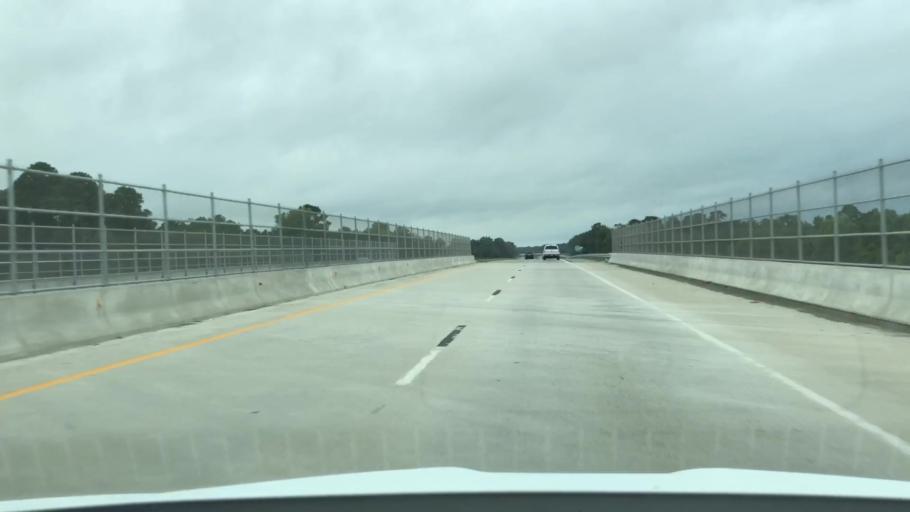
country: US
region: North Carolina
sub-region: Wayne County
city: Elroy
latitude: 35.3421
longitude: -77.8452
